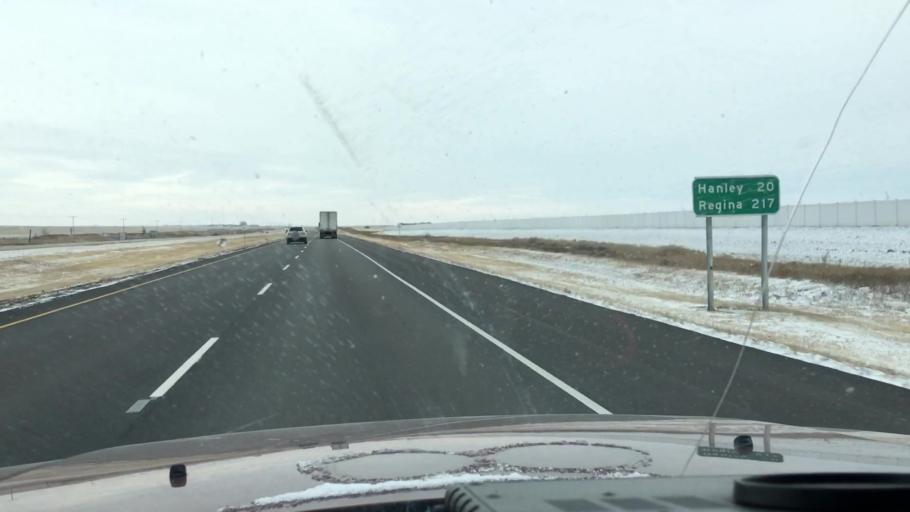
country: CA
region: Saskatchewan
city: Saskatoon
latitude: 51.8068
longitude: -106.4937
